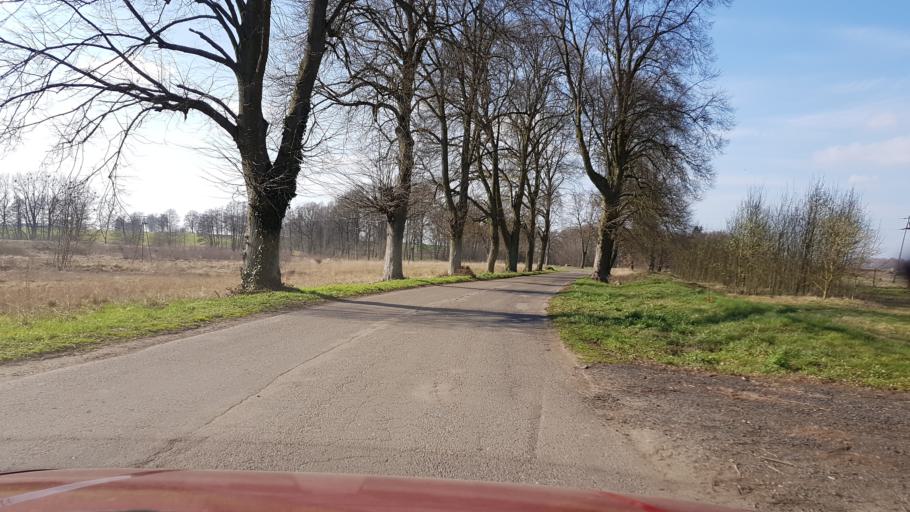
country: PL
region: West Pomeranian Voivodeship
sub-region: Powiat gryficki
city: Ploty
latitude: 53.7082
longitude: 15.2703
